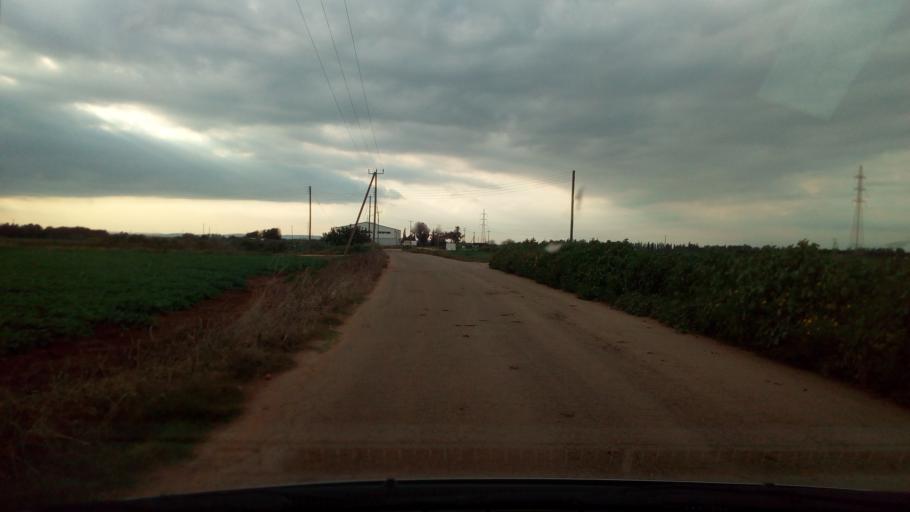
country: CY
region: Ammochostos
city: Avgorou
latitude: 34.9960
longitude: 33.8227
